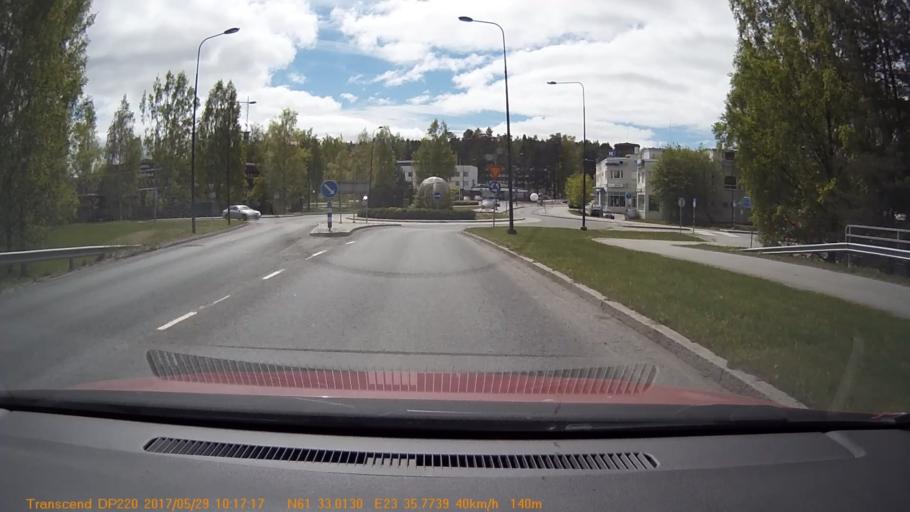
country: FI
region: Pirkanmaa
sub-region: Tampere
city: Yloejaervi
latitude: 61.5506
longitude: 23.5969
